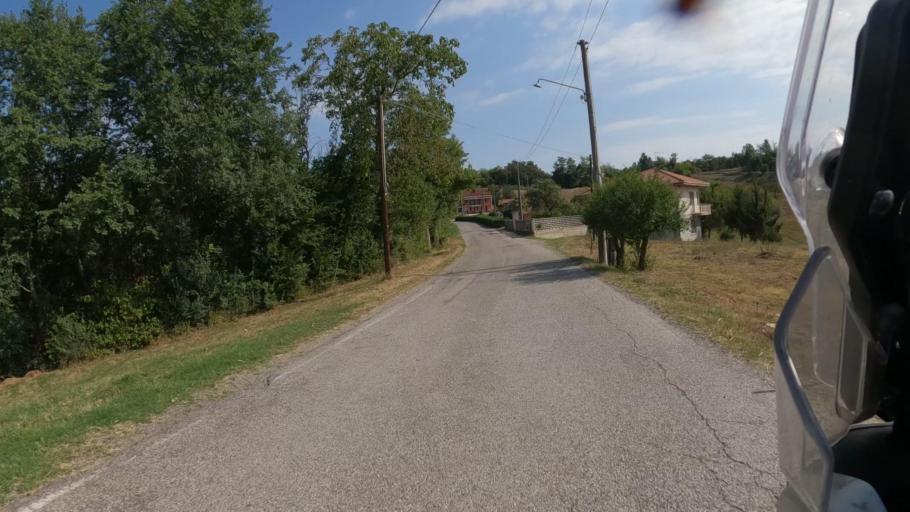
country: IT
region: Piedmont
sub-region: Provincia di Alessandria
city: Altavilla Monferrato
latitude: 44.9727
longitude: 8.3874
